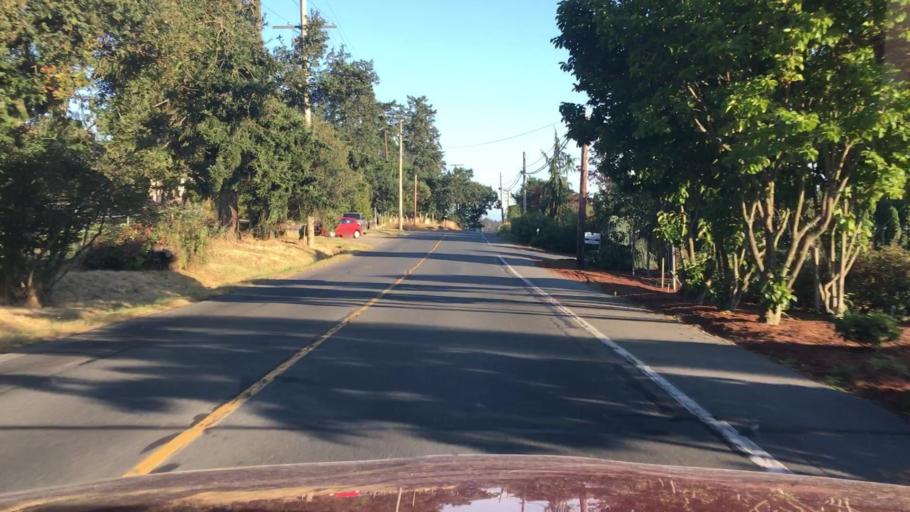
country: CA
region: British Columbia
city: Victoria
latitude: 48.4850
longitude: -123.3550
